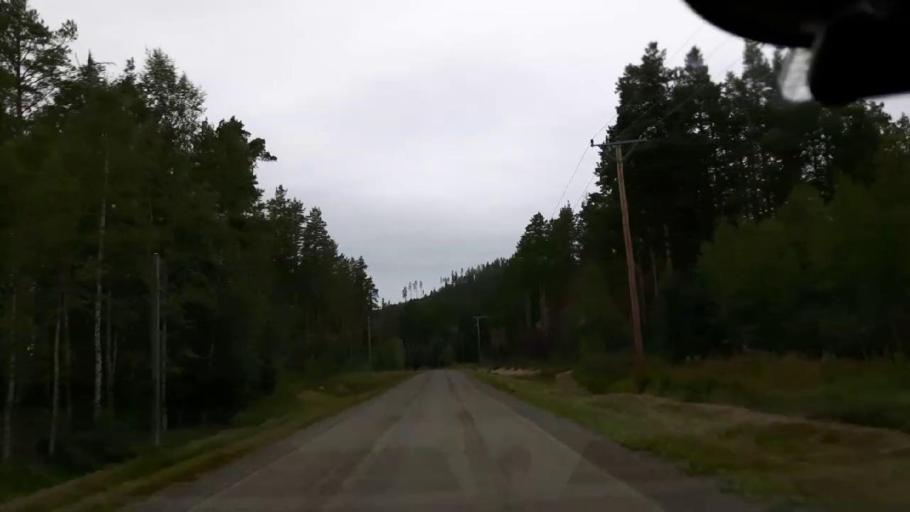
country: SE
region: Vaesternorrland
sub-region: Ange Kommun
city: Fransta
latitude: 62.7856
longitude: 16.0651
